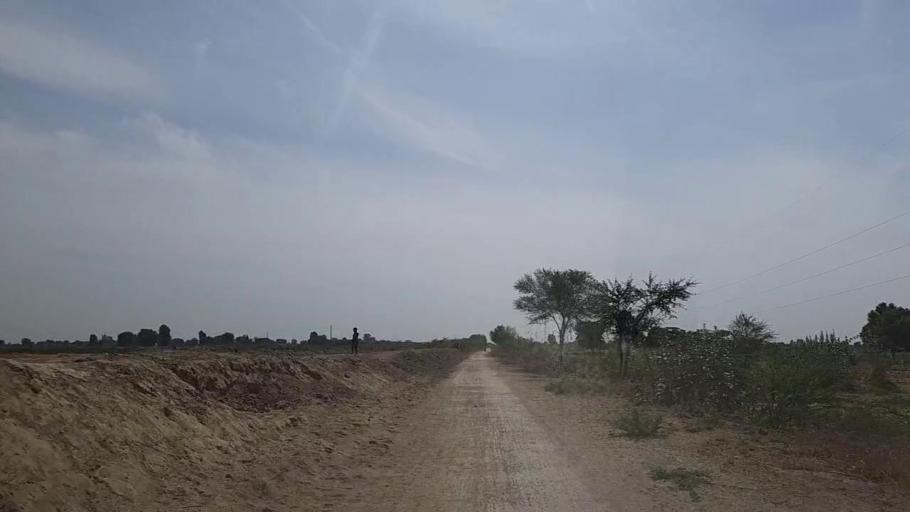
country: PK
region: Sindh
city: Kunri
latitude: 25.1945
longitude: 69.4620
